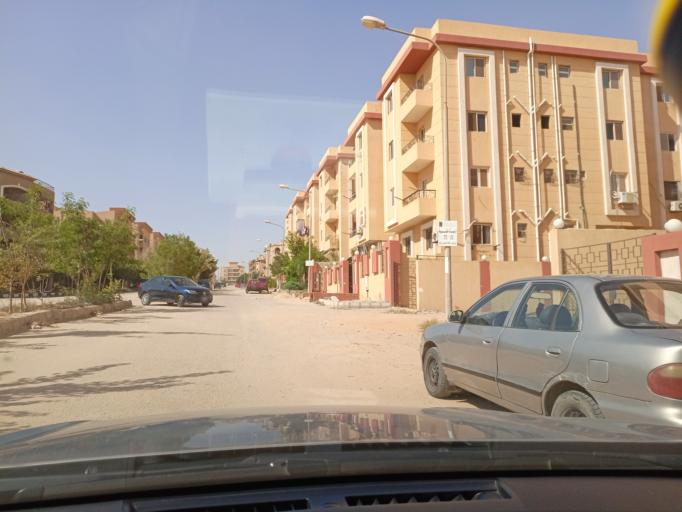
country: EG
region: Muhafazat al Qalyubiyah
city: Al Khankah
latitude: 30.2174
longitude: 31.4431
